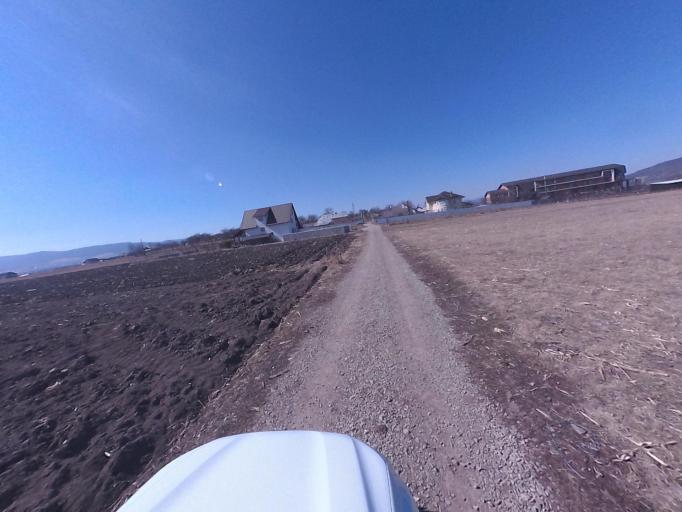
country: RO
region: Neamt
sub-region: Oras Targu Neamt
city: Humulesti
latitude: 47.1892
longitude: 26.3449
